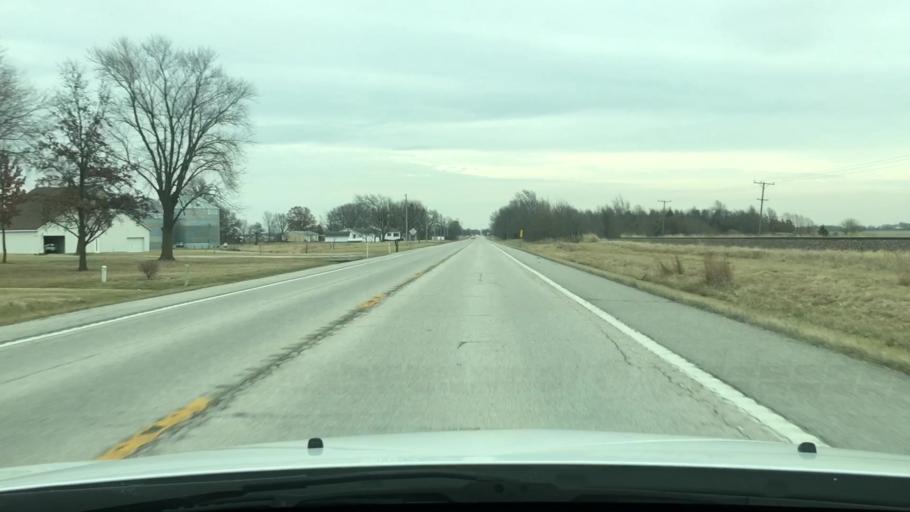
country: US
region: Missouri
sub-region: Audrain County
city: Vandalia
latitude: 39.2932
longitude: -91.5265
